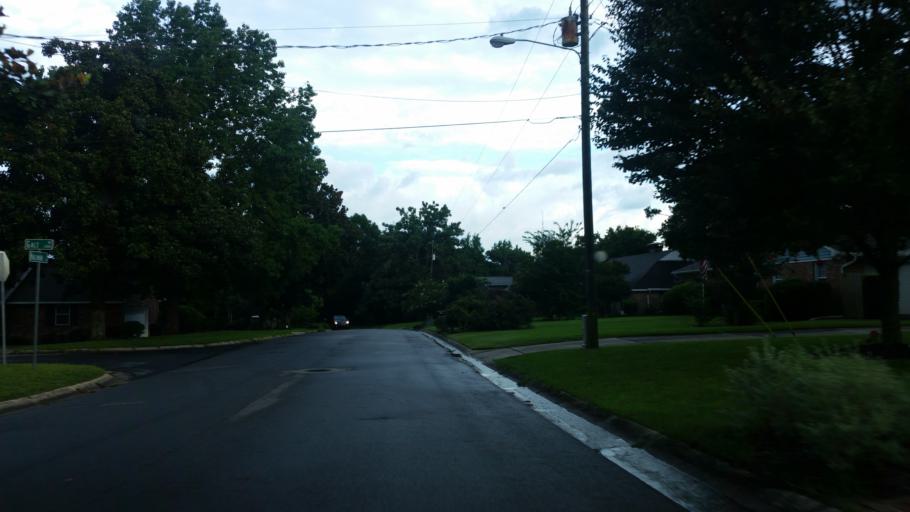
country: US
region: Florida
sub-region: Escambia County
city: Goulding
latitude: 30.4606
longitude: -87.1993
